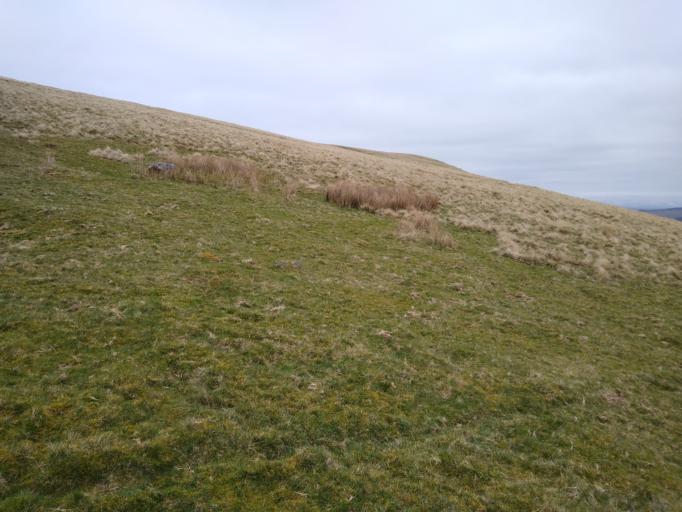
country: GB
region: England
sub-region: Cumbria
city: Keswick
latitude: 54.7059
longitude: -3.0428
